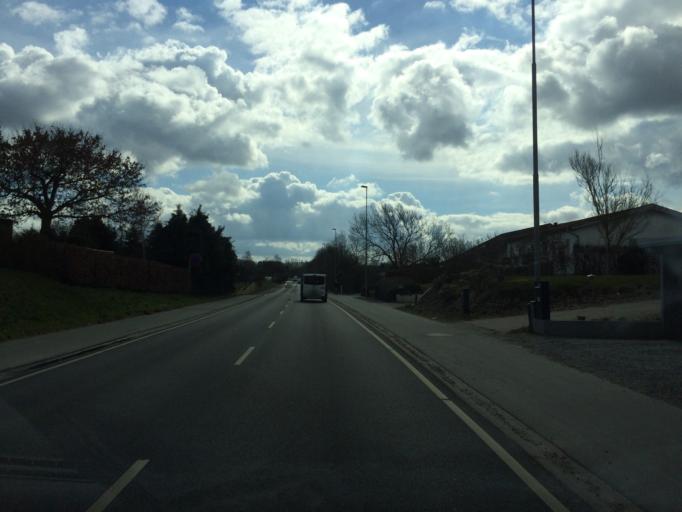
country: DK
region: South Denmark
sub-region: Nordfyns Kommune
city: Sonderso
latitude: 55.4024
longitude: 10.2608
